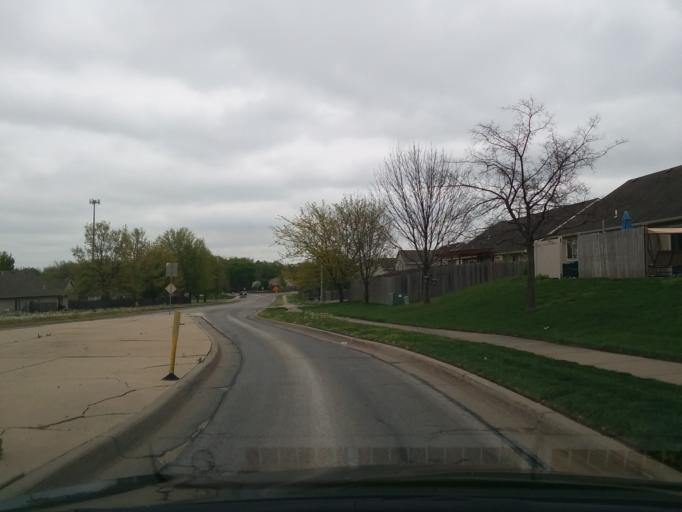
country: US
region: Kansas
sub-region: Douglas County
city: Lawrence
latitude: 38.9932
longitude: -95.2819
